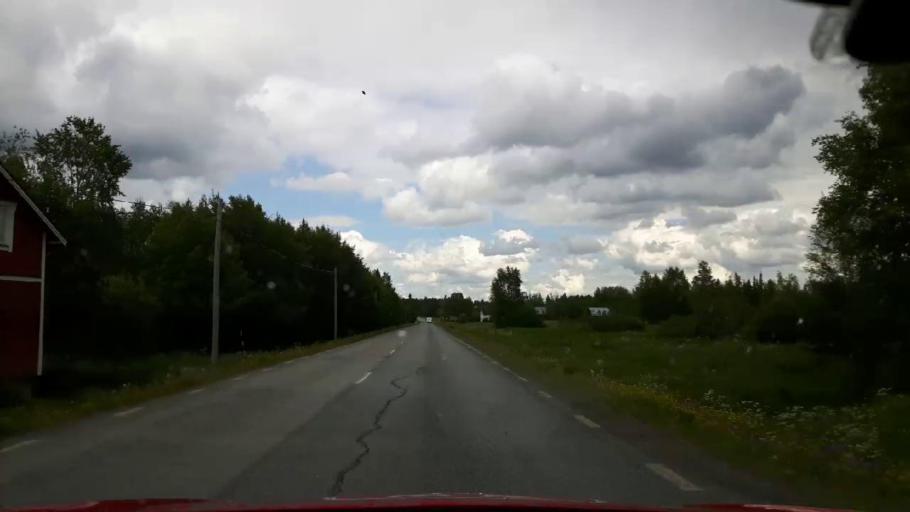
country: SE
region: Jaemtland
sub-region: Krokoms Kommun
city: Krokom
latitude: 63.5113
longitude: 14.2248
